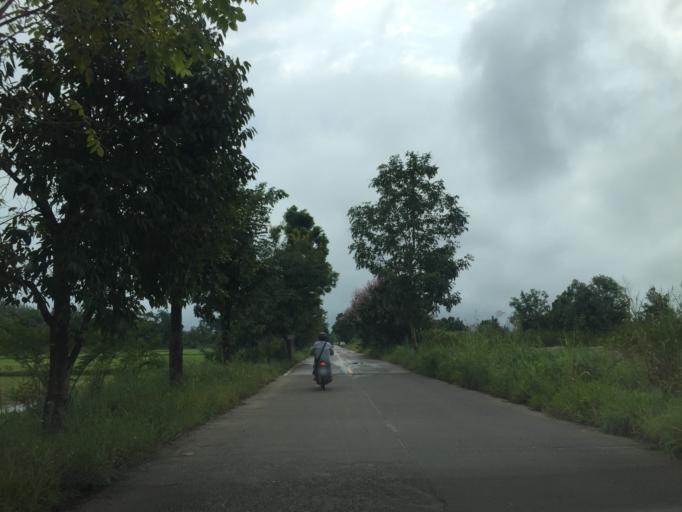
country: TH
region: Lamphun
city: Ban Thi
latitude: 18.6655
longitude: 99.0744
